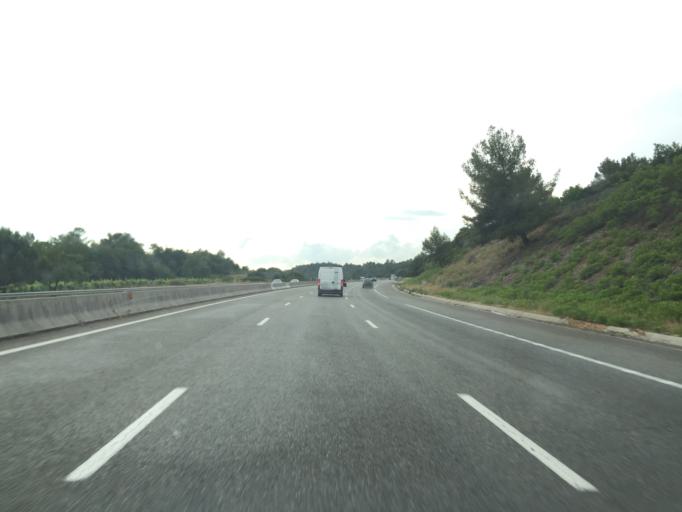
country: FR
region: Provence-Alpes-Cote d'Azur
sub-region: Departement du Var
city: Tourves
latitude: 43.4303
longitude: 5.9395
